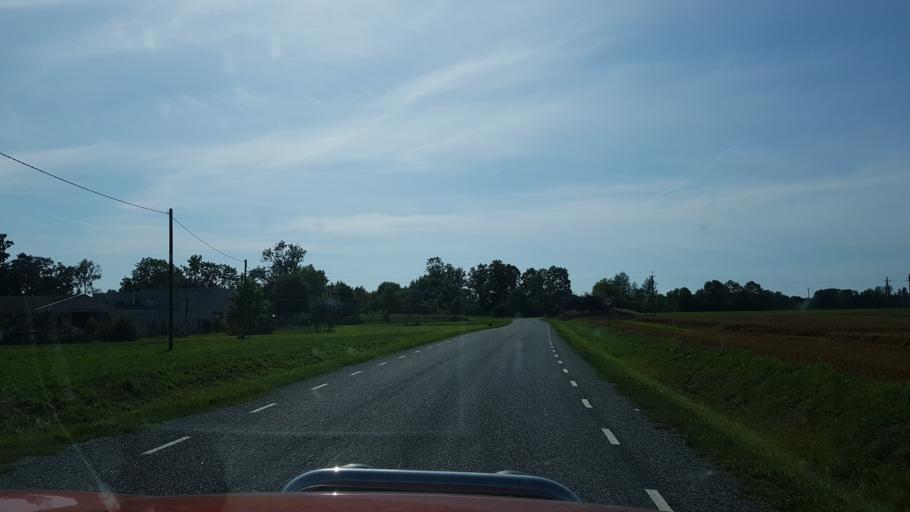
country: EE
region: Viljandimaa
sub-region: Viljandi linn
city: Viljandi
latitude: 58.3288
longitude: 25.5575
